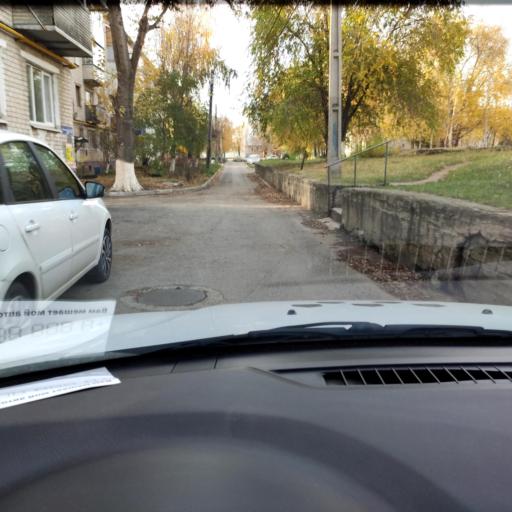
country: RU
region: Samara
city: Zhigulevsk
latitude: 53.4751
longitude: 49.4806
